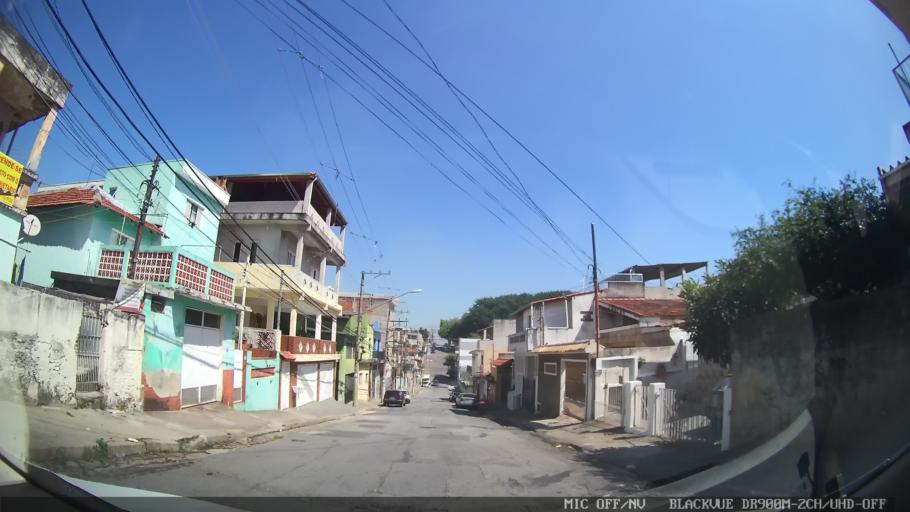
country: BR
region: Sao Paulo
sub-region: Sao Paulo
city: Sao Paulo
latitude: -23.4966
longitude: -46.6533
